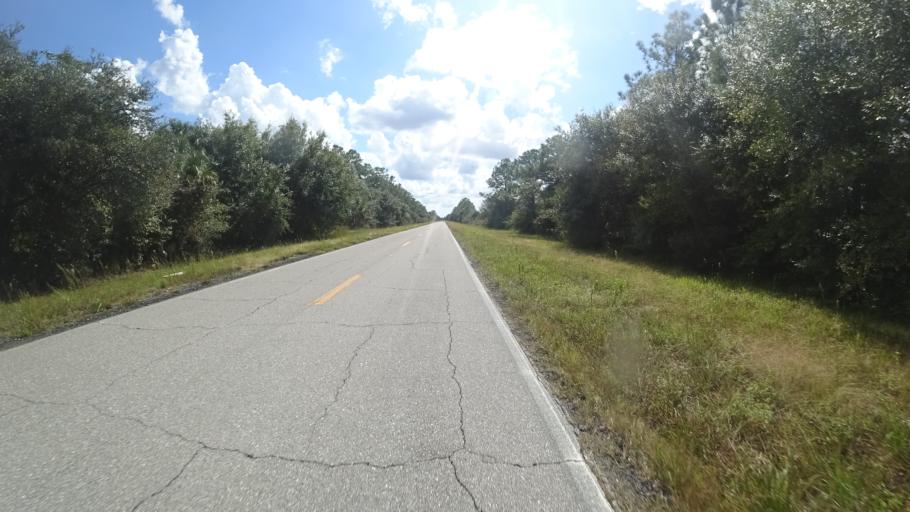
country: US
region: Florida
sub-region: Sarasota County
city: North Port
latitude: 27.2456
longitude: -82.1219
